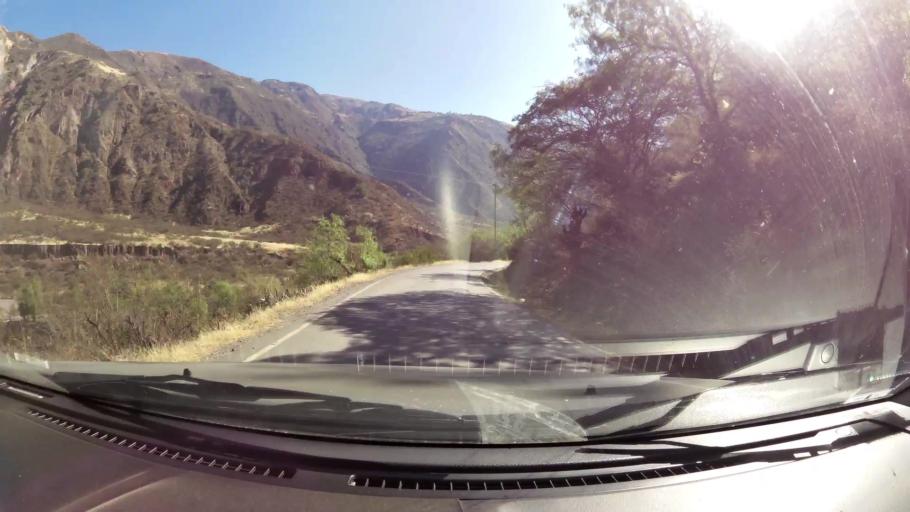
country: PE
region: Huancavelica
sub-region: Provincia de Acobamba
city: Pomacocha
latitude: -12.7653
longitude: -74.5097
